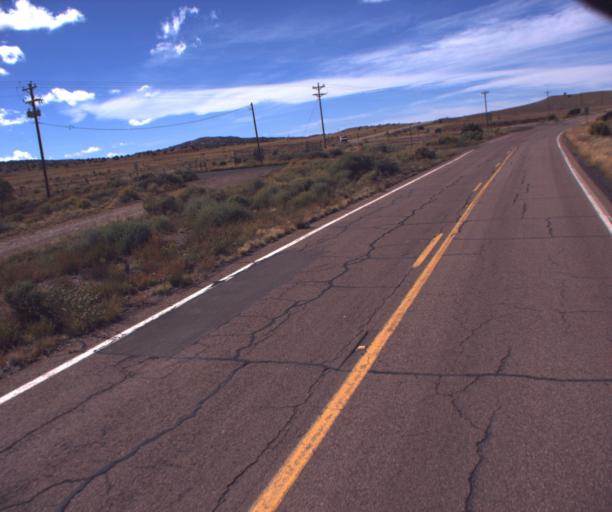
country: US
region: Arizona
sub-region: Apache County
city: Saint Johns
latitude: 34.4783
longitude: -109.6117
